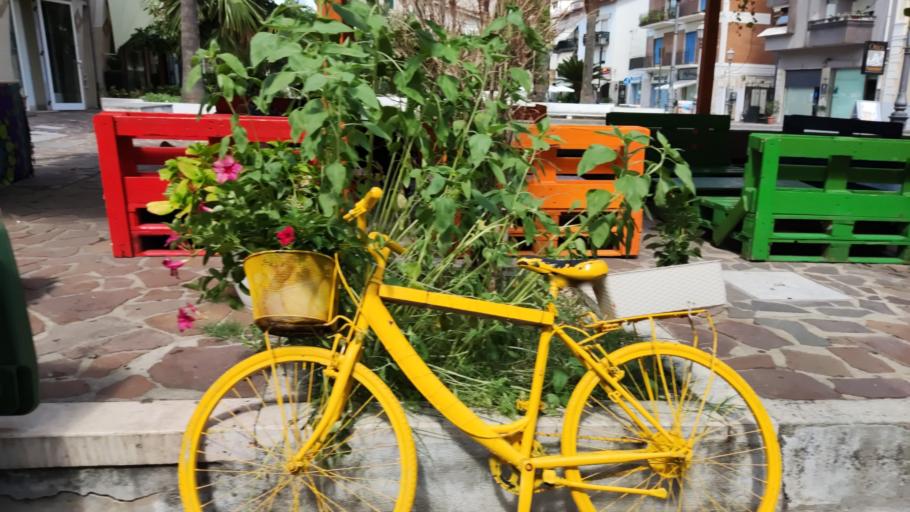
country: IT
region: Calabria
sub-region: Provincia di Reggio Calabria
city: Bagnara Calabra
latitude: 38.2866
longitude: 15.8024
